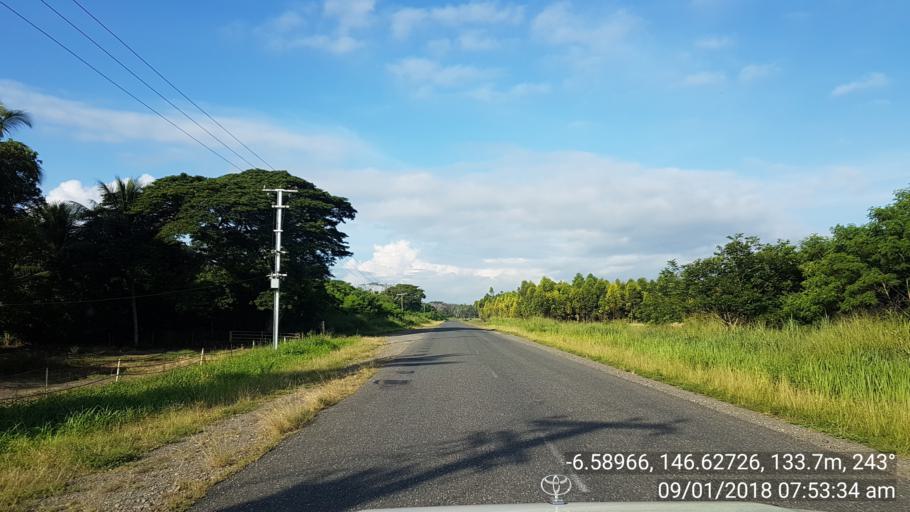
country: PG
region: Morobe
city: Lae
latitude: -6.5897
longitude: 146.6275
